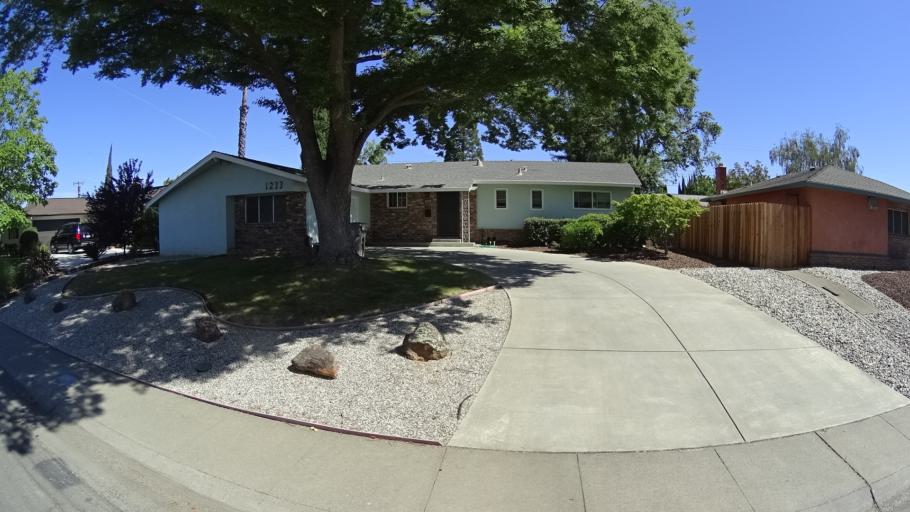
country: US
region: California
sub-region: Sacramento County
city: Parkway
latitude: 38.4976
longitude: -121.5139
